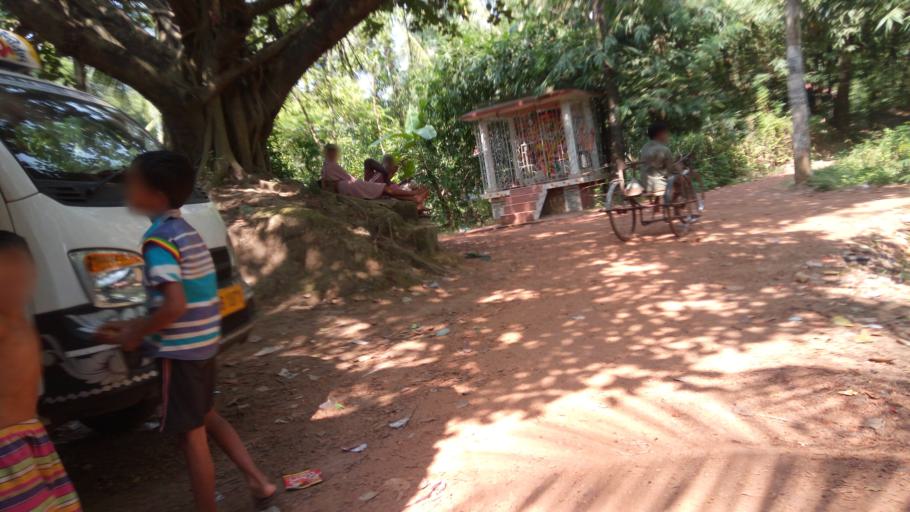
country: IN
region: West Bengal
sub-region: Purba Medinipur
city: Mahishadal
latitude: 22.1676
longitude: 87.9178
